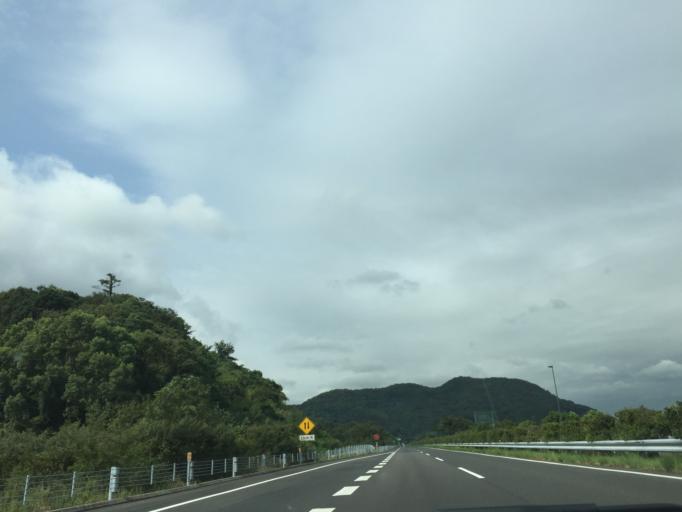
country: JP
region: Kagawa
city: Shido
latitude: 34.2762
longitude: 134.2755
